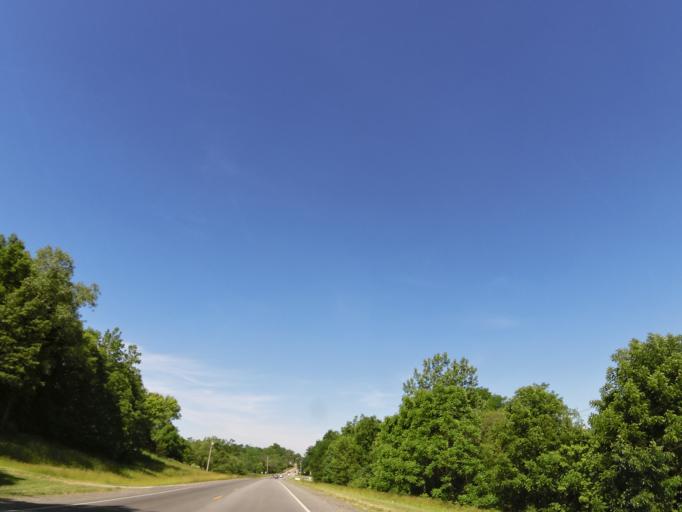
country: US
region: Illinois
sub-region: Vermilion County
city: Danville
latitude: 40.1329
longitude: -87.5692
